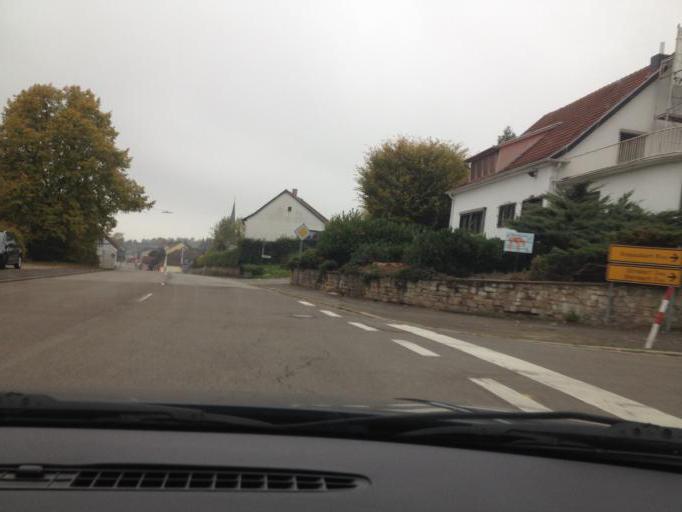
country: DE
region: Saarland
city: Eppelborn
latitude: 49.4476
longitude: 6.9650
